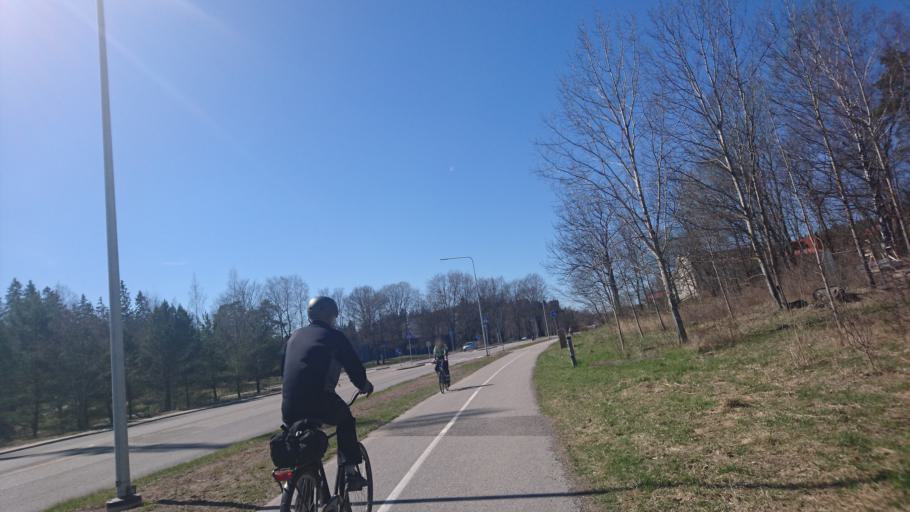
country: FI
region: Varsinais-Suomi
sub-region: Turku
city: Raisio
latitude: 60.4489
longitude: 22.1721
